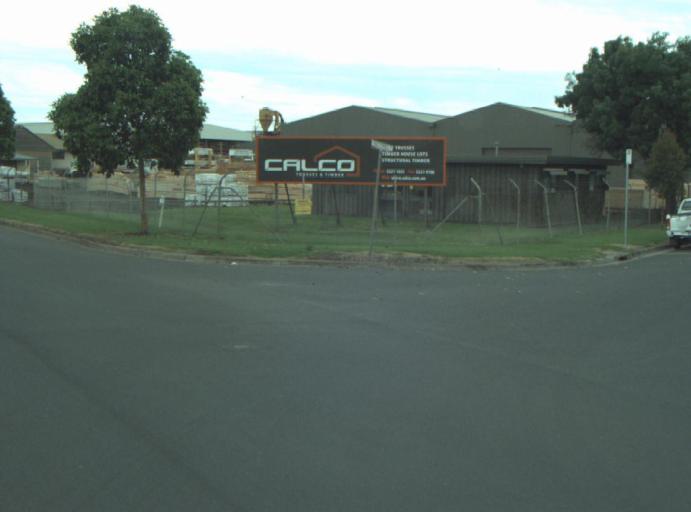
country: AU
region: Victoria
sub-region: Greater Geelong
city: Breakwater
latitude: -38.1664
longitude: 144.3621
